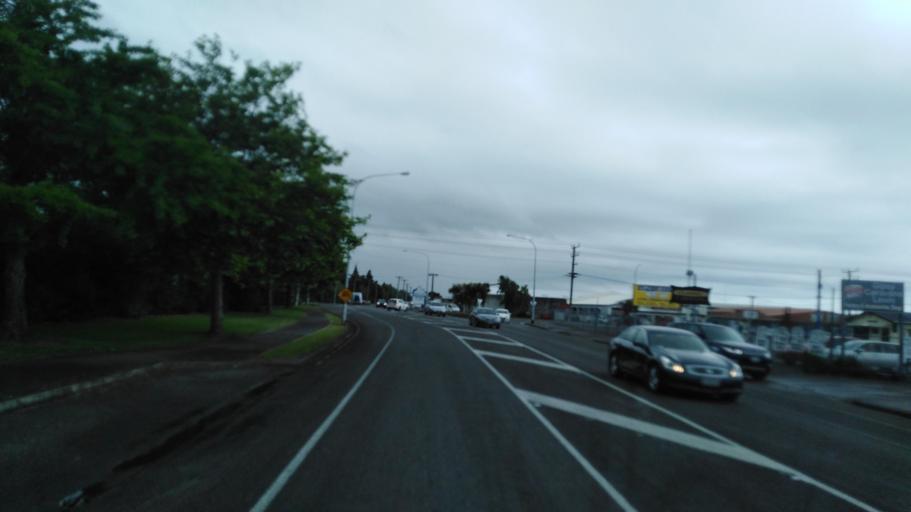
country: NZ
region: Manawatu-Wanganui
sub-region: Horowhenua District
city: Levin
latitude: -40.6324
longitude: 175.2763
